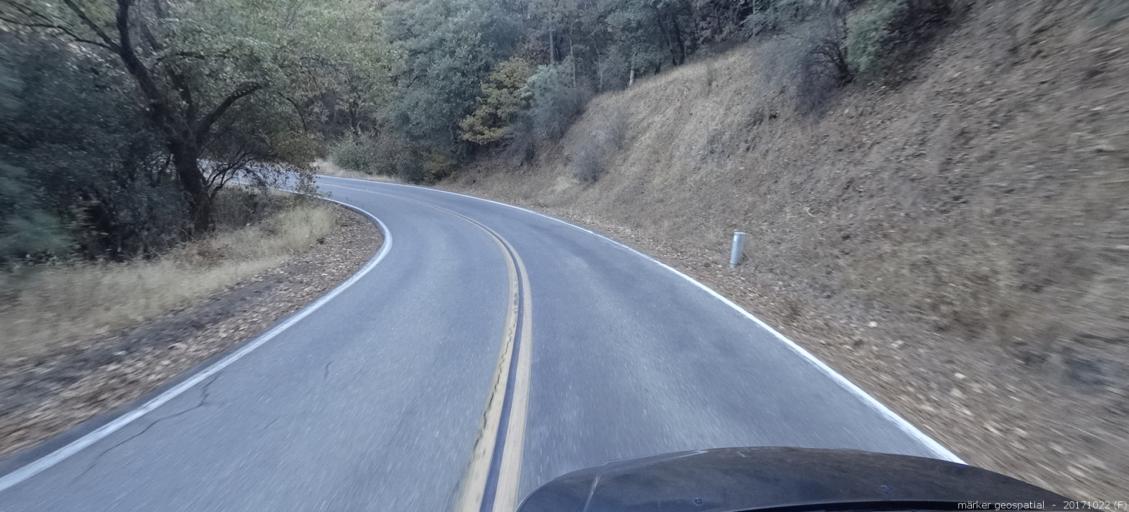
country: US
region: California
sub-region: Shasta County
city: Shasta Lake
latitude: 40.8766
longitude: -122.2403
